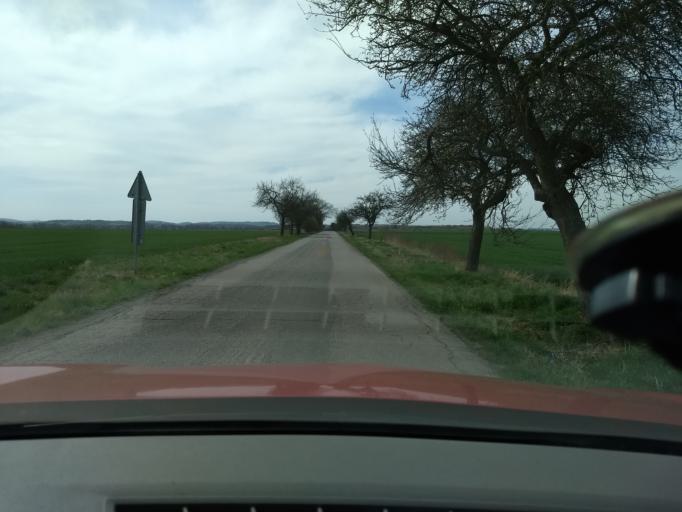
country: CZ
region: Central Bohemia
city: Rudna
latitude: 50.0512
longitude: 14.2184
